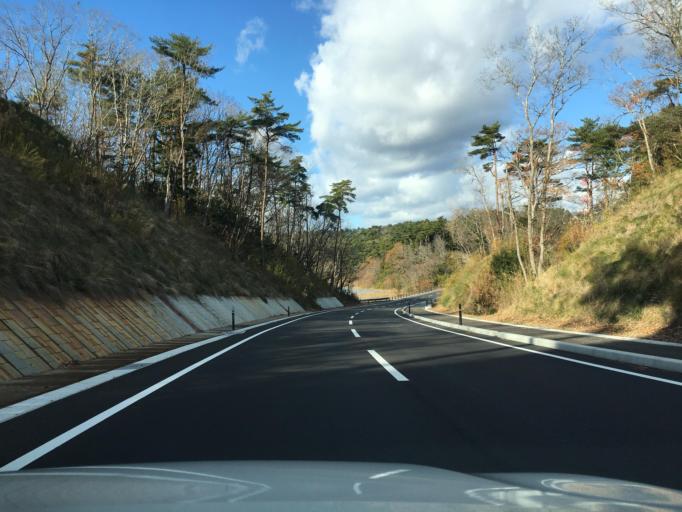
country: JP
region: Fukushima
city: Namie
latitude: 37.3078
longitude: 141.0142
